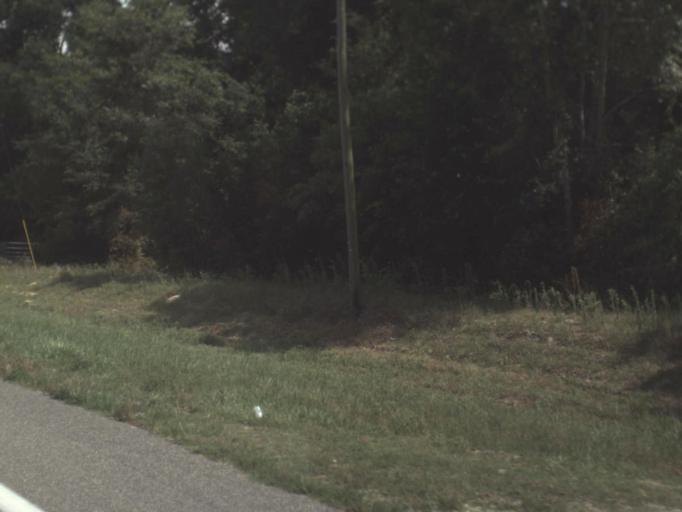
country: US
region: Florida
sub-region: Lafayette County
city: Mayo
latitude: 29.9634
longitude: -82.9721
